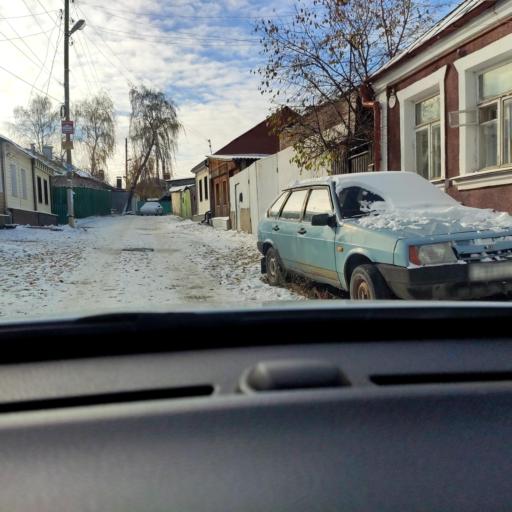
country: RU
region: Voronezj
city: Voronezh
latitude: 51.6493
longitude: 39.1994
